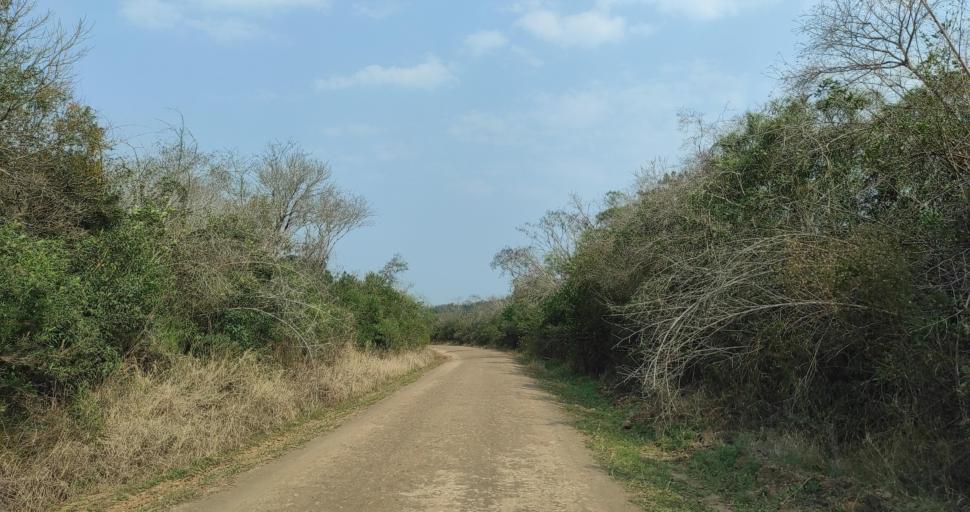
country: AR
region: Misiones
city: Cerro Cora
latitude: -27.5947
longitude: -55.5782
